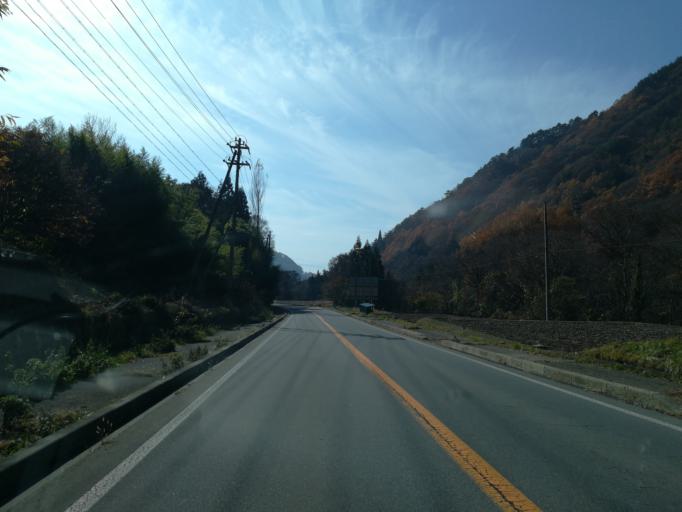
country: JP
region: Nagano
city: Ueda
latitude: 36.4558
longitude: 138.3330
